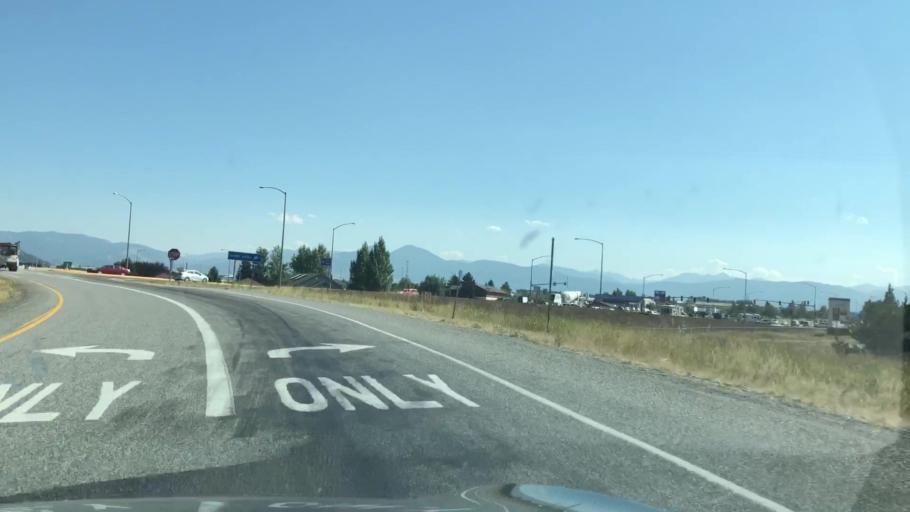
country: US
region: Montana
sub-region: Gallatin County
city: Bozeman
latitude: 45.7138
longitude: -111.0658
